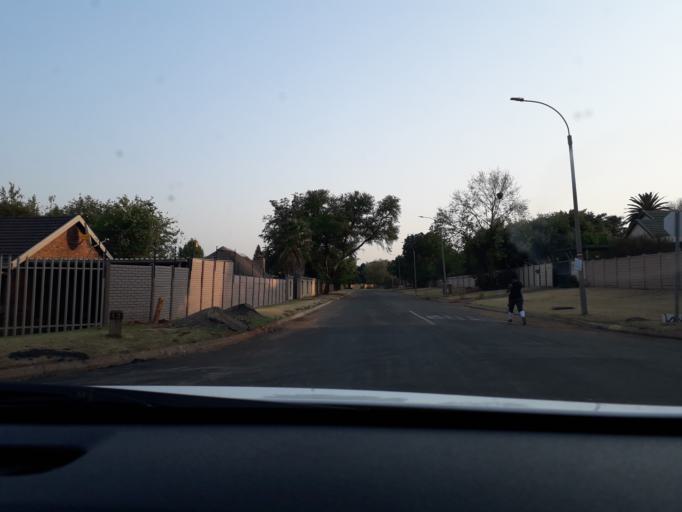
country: ZA
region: Gauteng
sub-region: City of Johannesburg Metropolitan Municipality
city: Modderfontein
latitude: -26.0656
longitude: 28.2012
